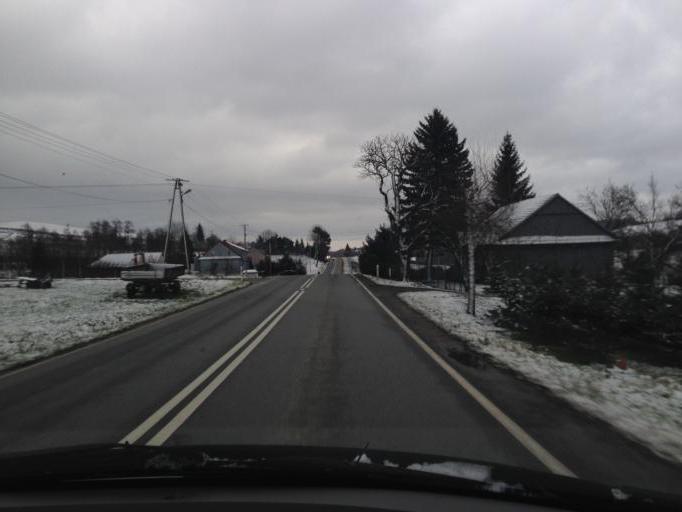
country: PL
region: Lesser Poland Voivodeship
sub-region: Powiat tarnowski
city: Siemiechow
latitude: 49.8554
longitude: 20.8843
